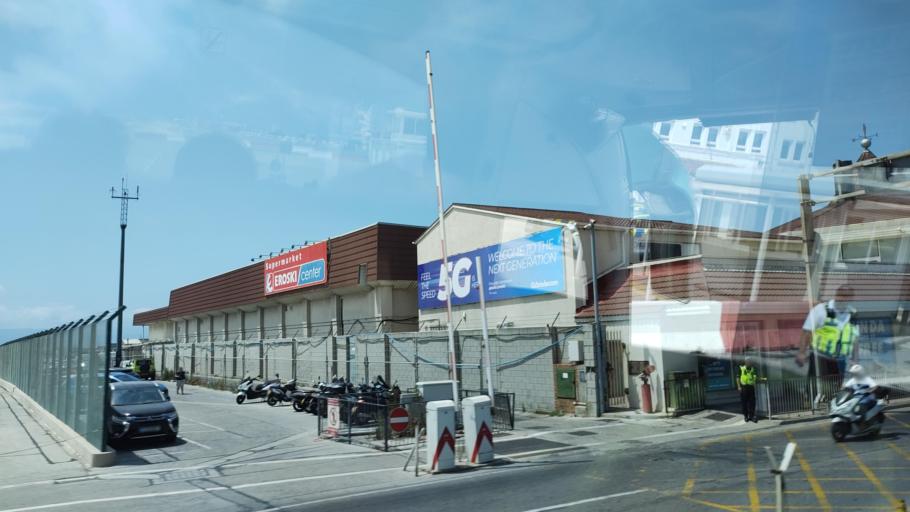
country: GI
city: Gibraltar
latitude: 36.1523
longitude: -5.3486
